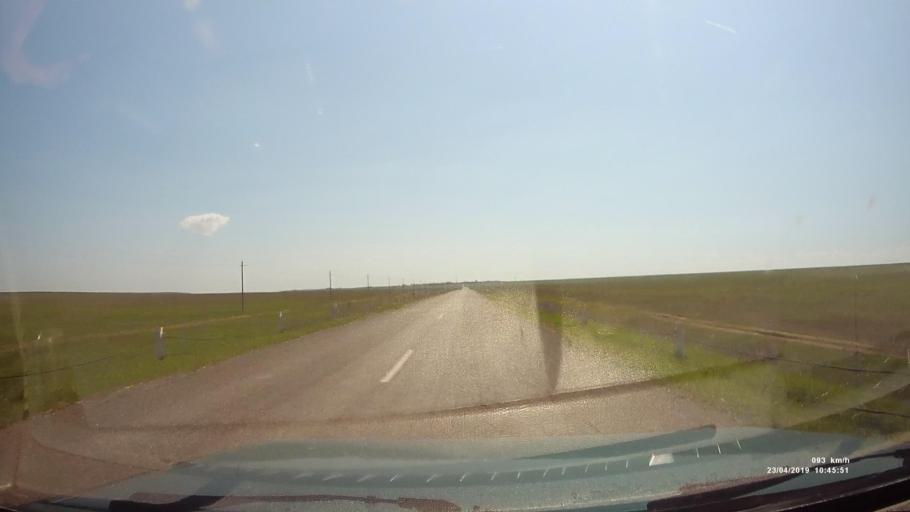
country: RU
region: Kalmykiya
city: Yashalta
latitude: 46.4481
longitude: 42.6810
